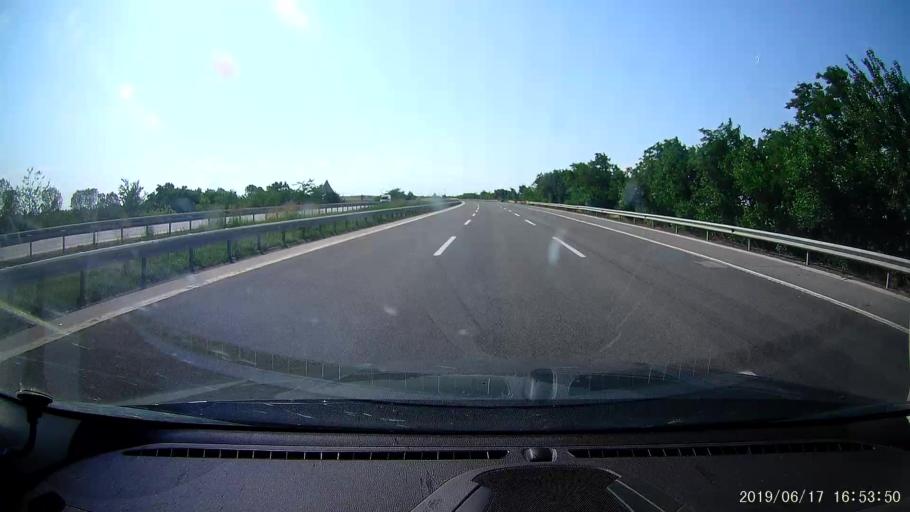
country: TR
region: Kirklareli
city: Inece
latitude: 41.5687
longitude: 27.0129
